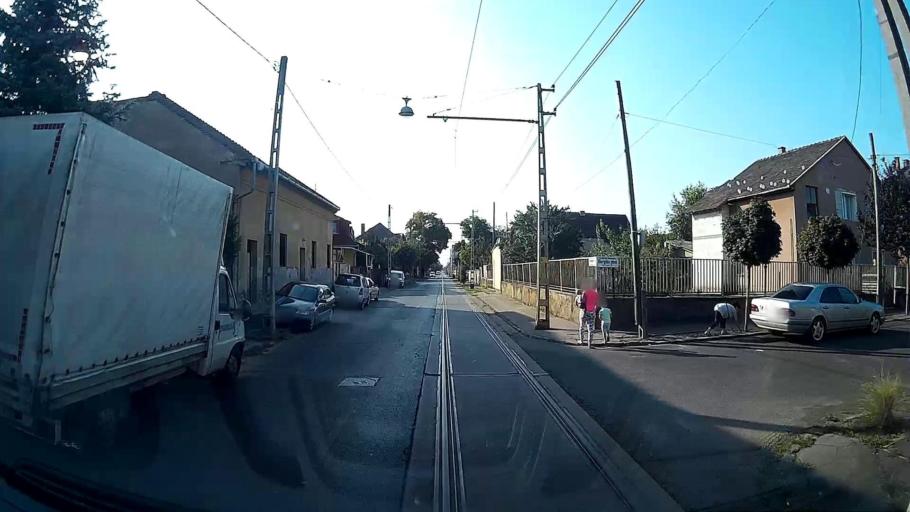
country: HU
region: Budapest
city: Budapest XX. keruelet
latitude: 47.4278
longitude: 19.1121
